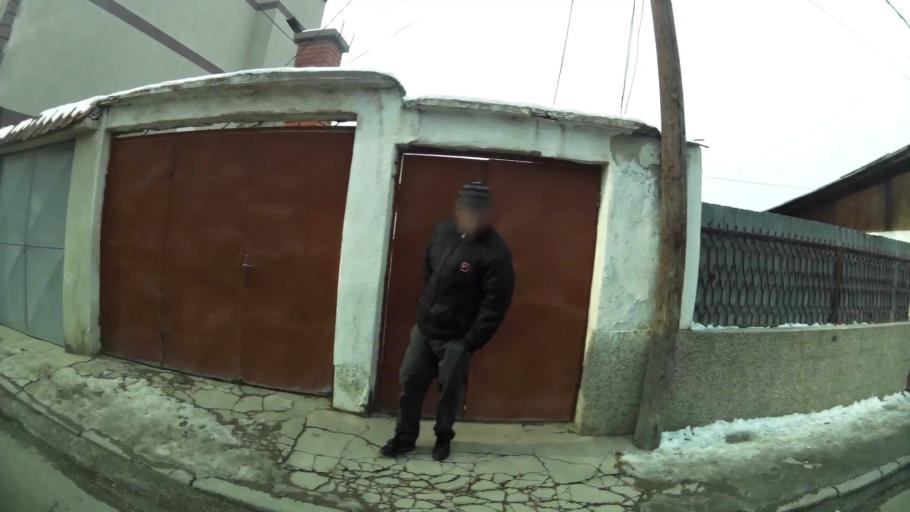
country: MK
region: Cair
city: Cair
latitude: 42.0073
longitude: 21.4467
